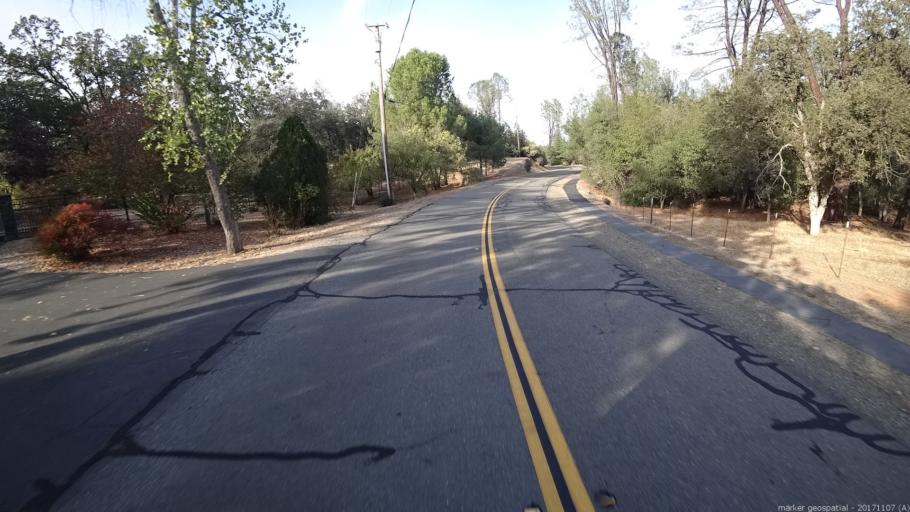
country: US
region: California
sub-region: Shasta County
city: Shasta
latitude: 40.5206
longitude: -122.4653
